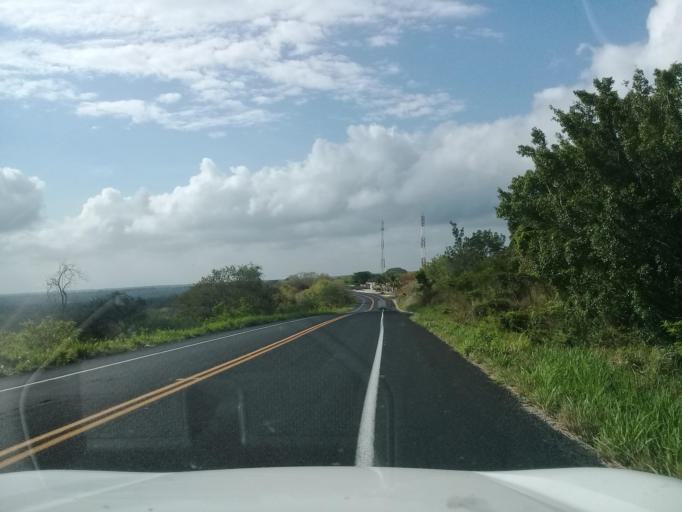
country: MX
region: Veracruz
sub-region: Emiliano Zapata
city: Plan del Rio
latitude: 19.4155
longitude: -96.6541
